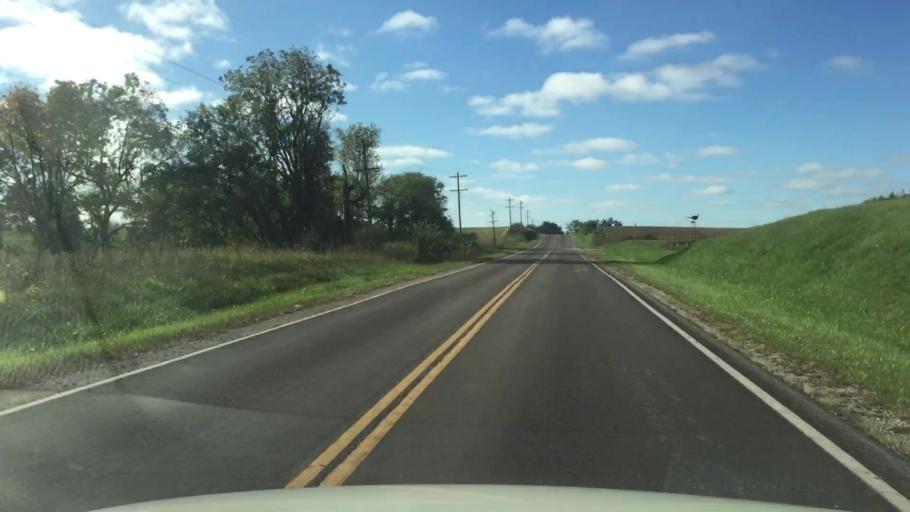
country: US
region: Missouri
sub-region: Howard County
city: New Franklin
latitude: 39.0692
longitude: -92.7460
